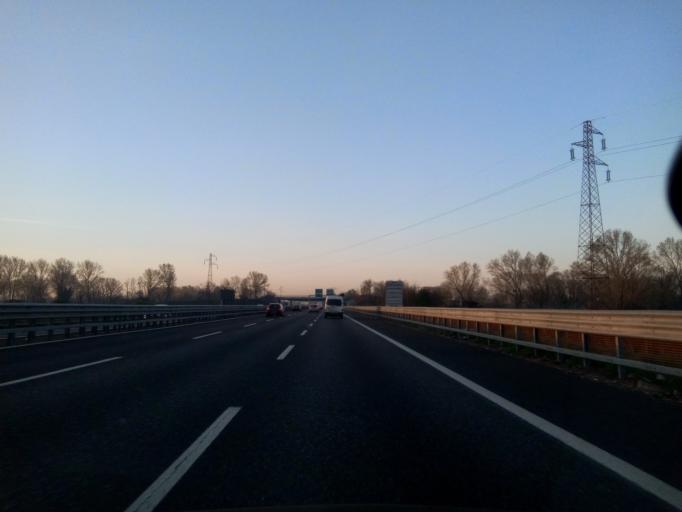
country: IT
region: Lombardy
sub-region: Citta metropolitana di Milano
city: Trezzano sul Naviglio
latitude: 45.4393
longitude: 9.0738
